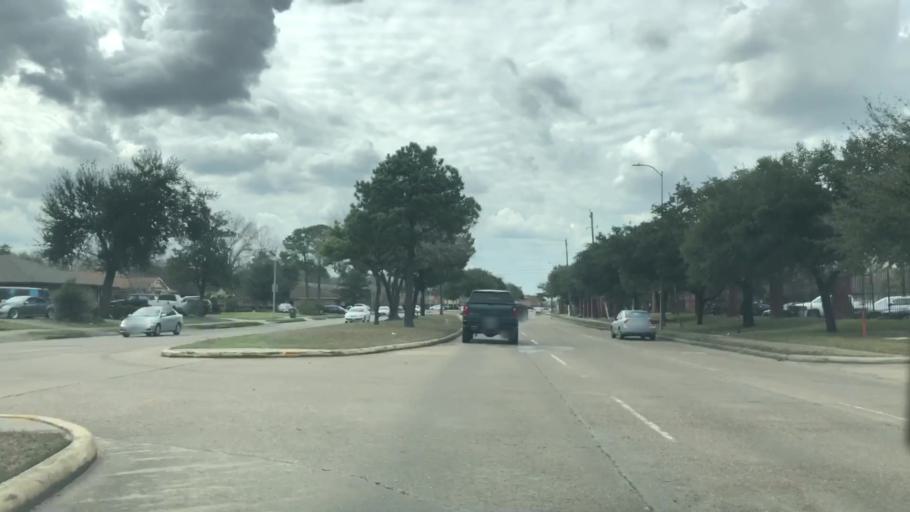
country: US
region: Texas
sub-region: Harris County
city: Bellaire
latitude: 29.6911
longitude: -95.5164
